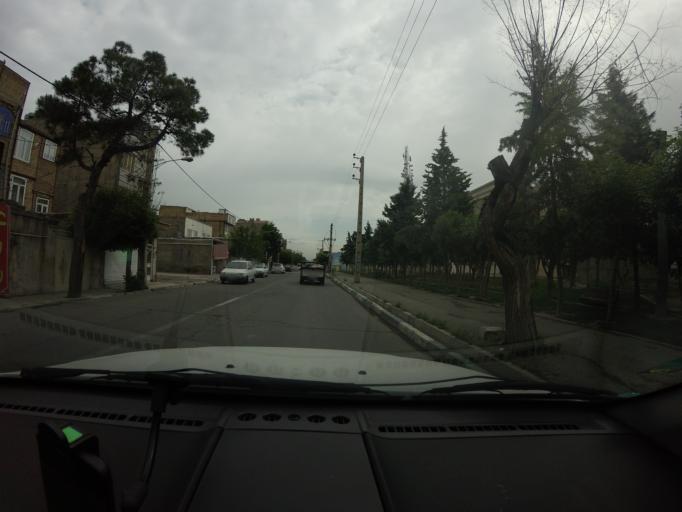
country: IR
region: Tehran
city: Eslamshahr
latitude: 35.5424
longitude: 51.2335
